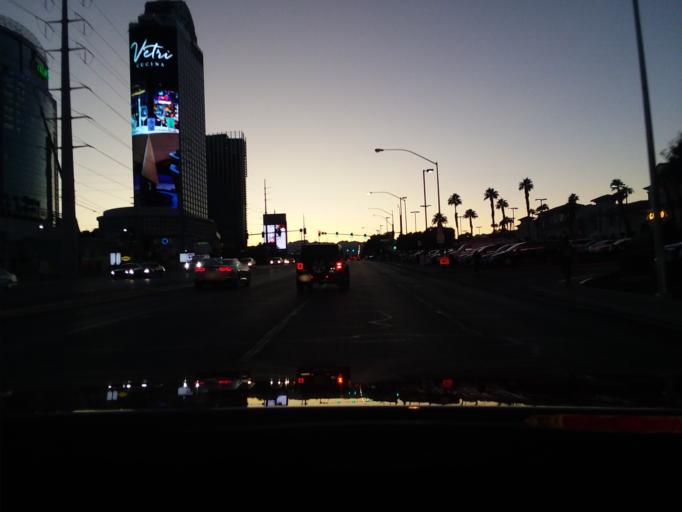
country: US
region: Nevada
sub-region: Clark County
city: Paradise
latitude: 36.1157
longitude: -115.1911
